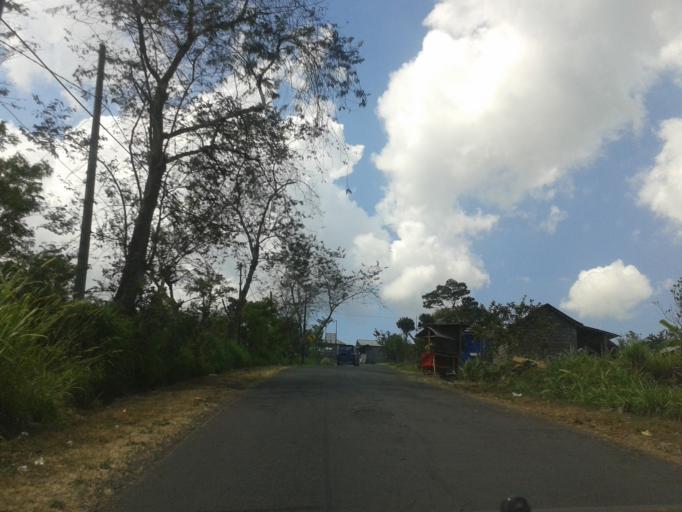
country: ID
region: Bali
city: Banjar Kedisan
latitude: -8.2819
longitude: 115.3505
